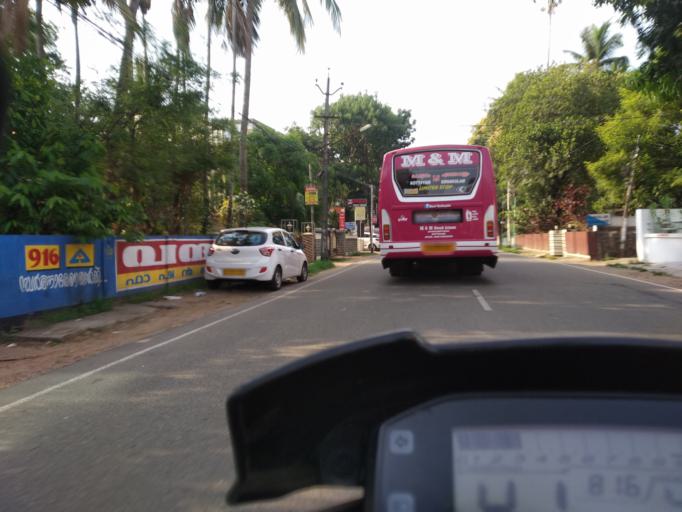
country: IN
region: Kerala
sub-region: Alappuzha
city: Arukutti
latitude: 9.9416
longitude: 76.3504
